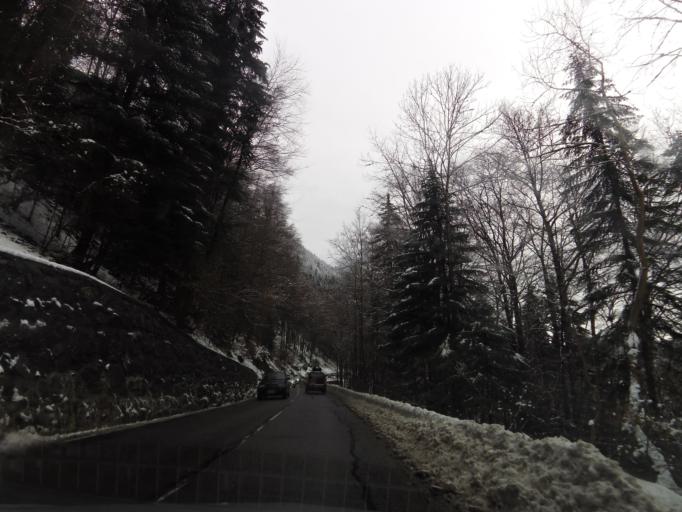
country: FR
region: Rhone-Alpes
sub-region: Departement de la Haute-Savoie
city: Taninges
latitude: 46.1252
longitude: 6.6226
